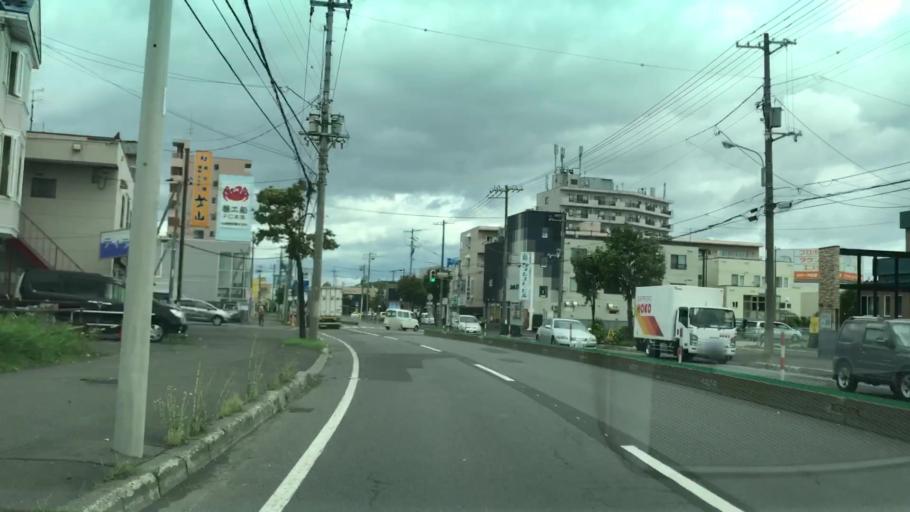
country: JP
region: Hokkaido
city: Sapporo
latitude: 42.9952
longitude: 141.4416
